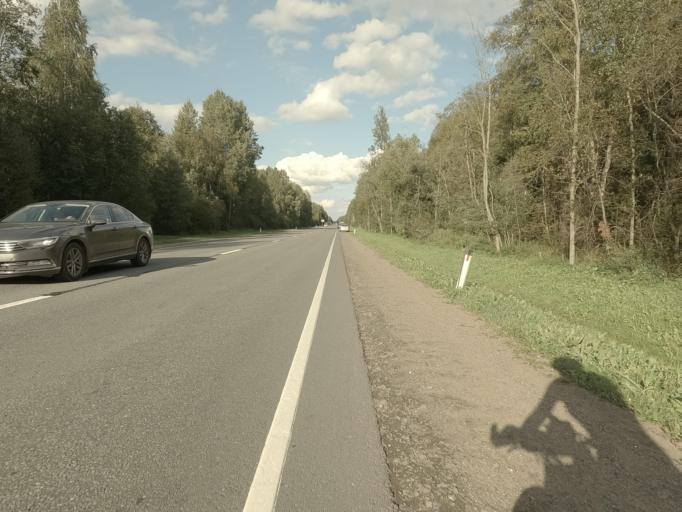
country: RU
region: Leningrad
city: Mga
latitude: 59.6892
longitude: 30.9706
